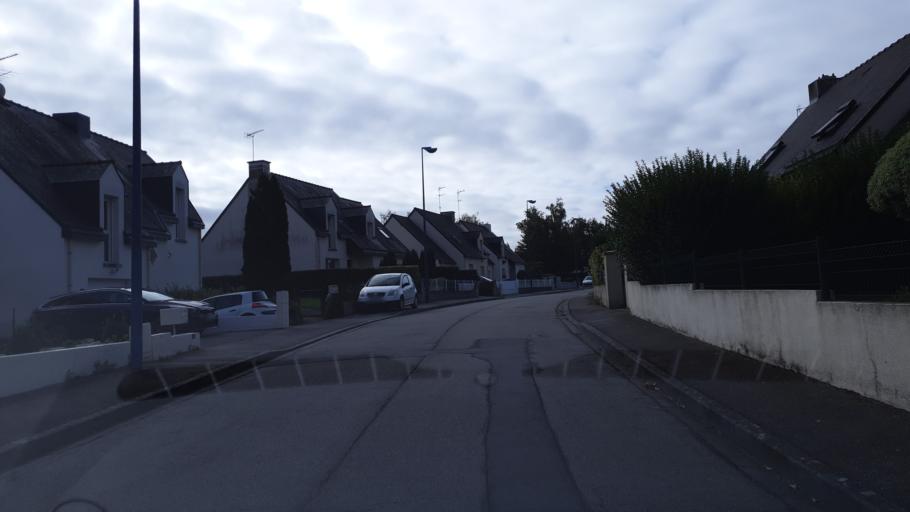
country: FR
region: Brittany
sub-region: Departement d'Ille-et-Vilaine
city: Janze
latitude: 47.9631
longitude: -1.4900
